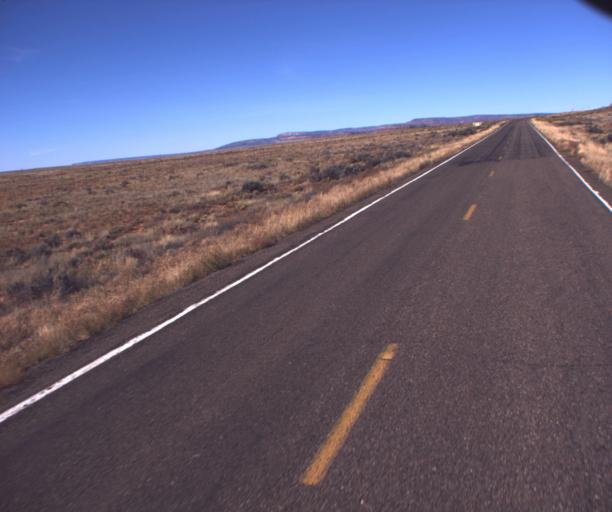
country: US
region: Arizona
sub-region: Coconino County
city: Fredonia
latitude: 36.9281
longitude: -112.4830
